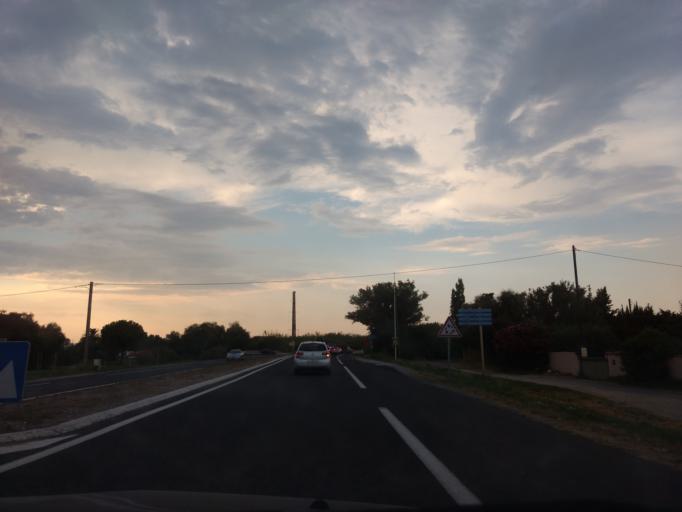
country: FR
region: Languedoc-Roussillon
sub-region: Departement des Pyrenees-Orientales
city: Sainte-Marie-Plage
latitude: 42.7308
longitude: 3.0271
